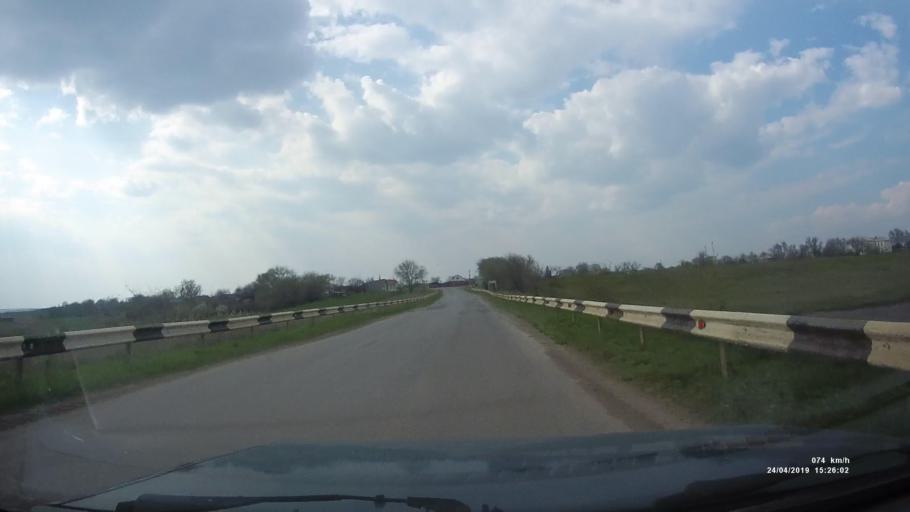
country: RU
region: Rostov
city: Remontnoye
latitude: 46.5559
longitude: 43.0380
